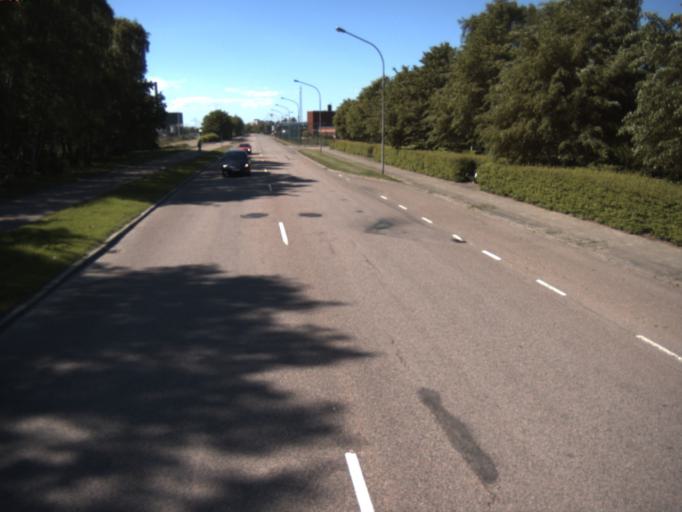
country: SE
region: Skane
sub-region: Helsingborg
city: Helsingborg
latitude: 56.0052
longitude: 12.7278
